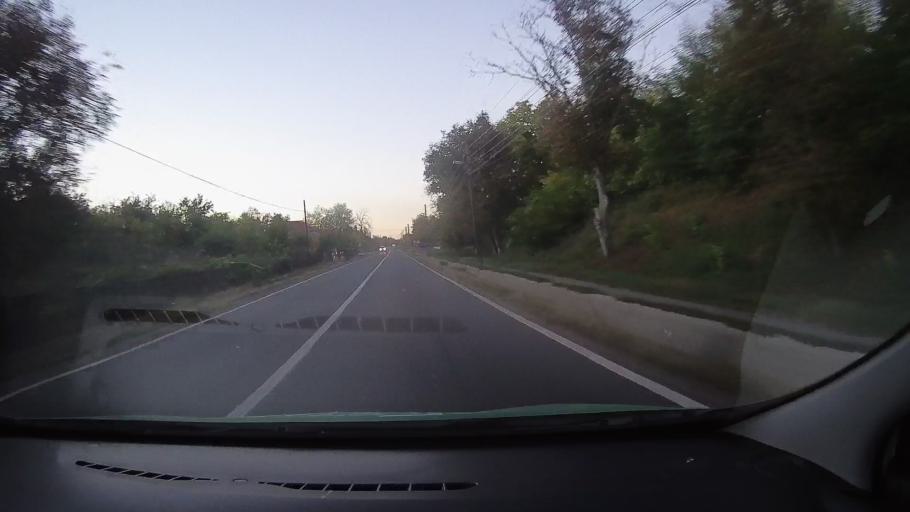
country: RO
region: Bihor
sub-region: Comuna Tarcea
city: Tarcea
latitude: 47.4613
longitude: 22.1690
